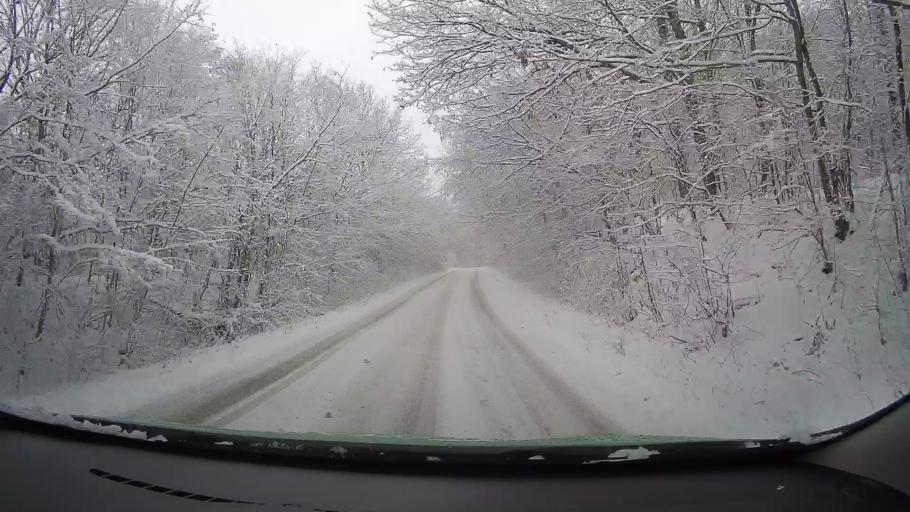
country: RO
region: Hunedoara
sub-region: Municipiul Deva
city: Deva
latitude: 45.8576
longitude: 22.8820
